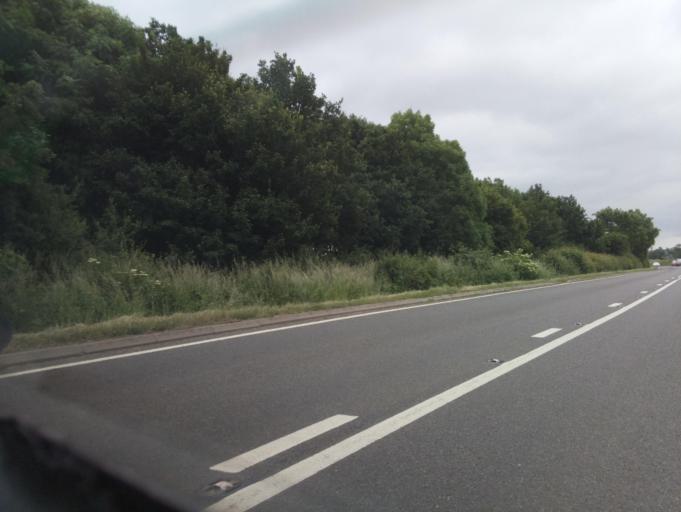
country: GB
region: England
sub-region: Leicestershire
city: Melton Mowbray
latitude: 52.7343
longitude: -0.8502
